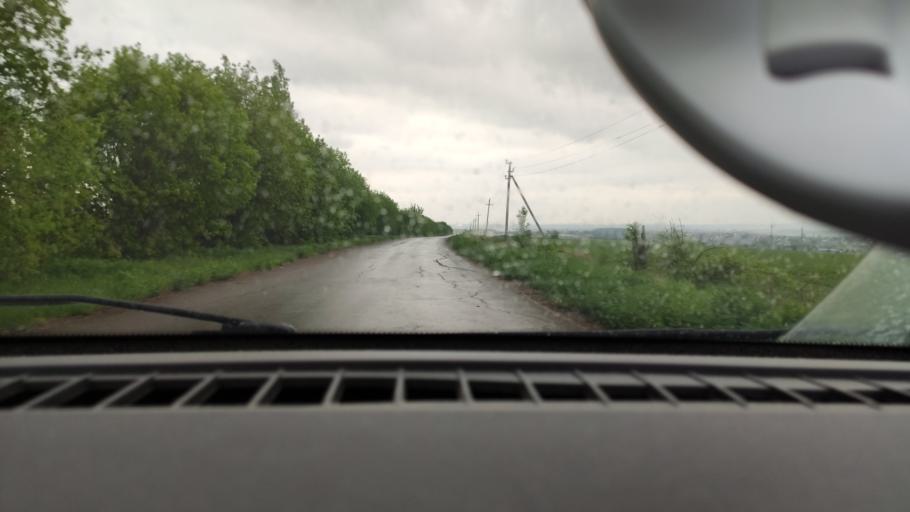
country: RU
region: Perm
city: Gamovo
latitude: 57.8540
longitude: 56.0801
